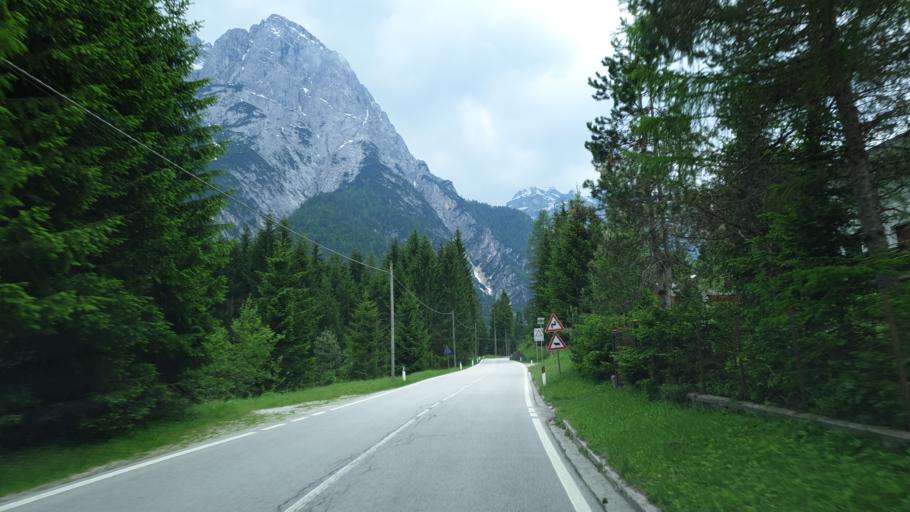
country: IT
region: Veneto
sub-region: Provincia di Belluno
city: Auronzo
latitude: 46.5556
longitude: 12.3386
